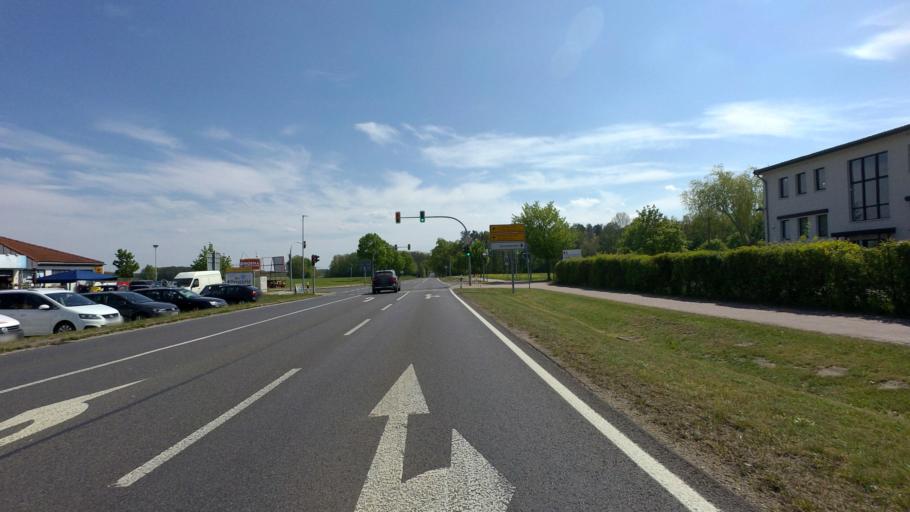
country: DE
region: Brandenburg
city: Tschernitz
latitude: 51.6027
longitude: 14.6107
